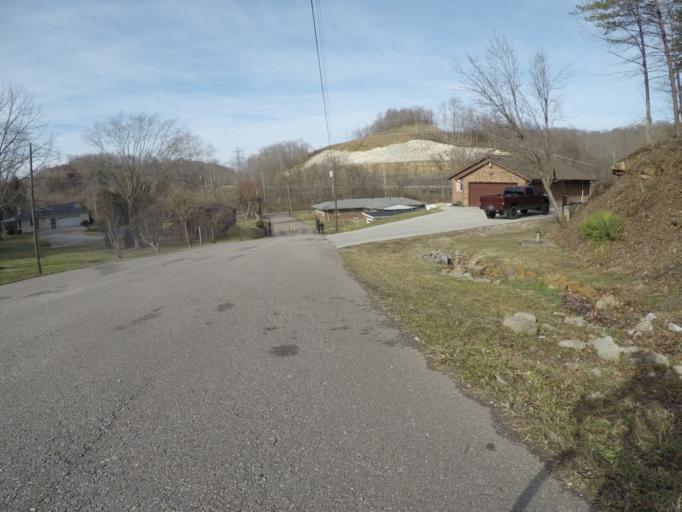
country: US
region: West Virginia
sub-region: Cabell County
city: Huntington
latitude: 38.3859
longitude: -82.3918
